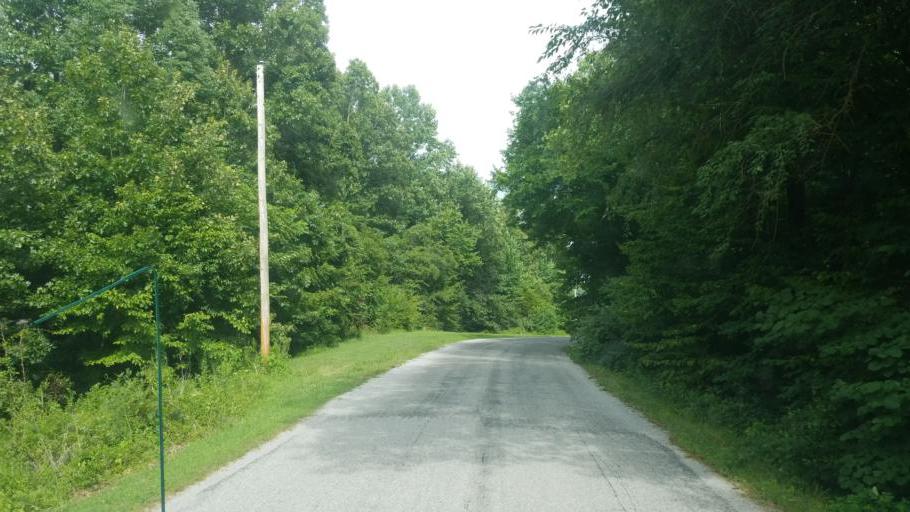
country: US
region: Illinois
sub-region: Union County
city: Cobden
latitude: 37.6123
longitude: -89.3457
